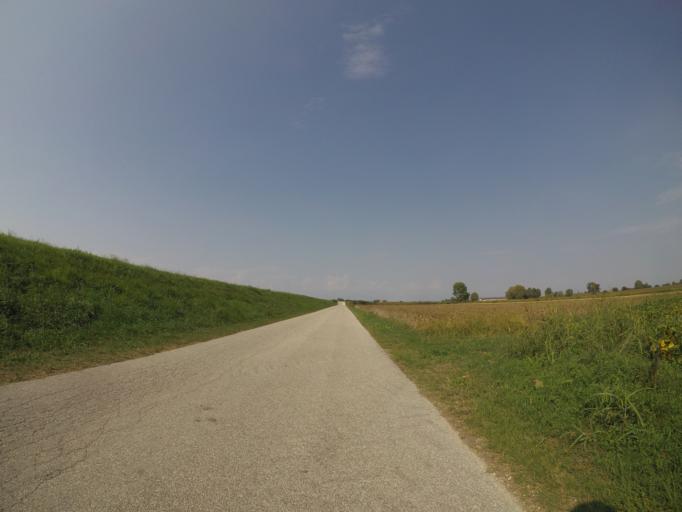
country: IT
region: Friuli Venezia Giulia
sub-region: Provincia di Udine
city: Camino al Tagliamento
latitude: 45.9328
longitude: 12.9214
